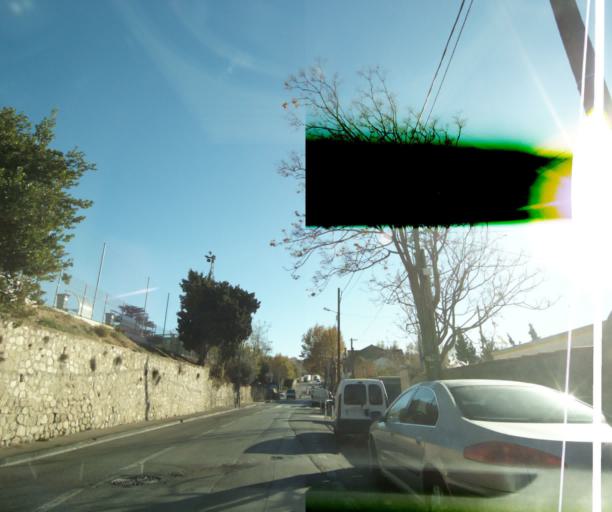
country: FR
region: Provence-Alpes-Cote d'Azur
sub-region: Departement des Bouches-du-Rhone
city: Marseille 15
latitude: 43.3520
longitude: 5.3539
